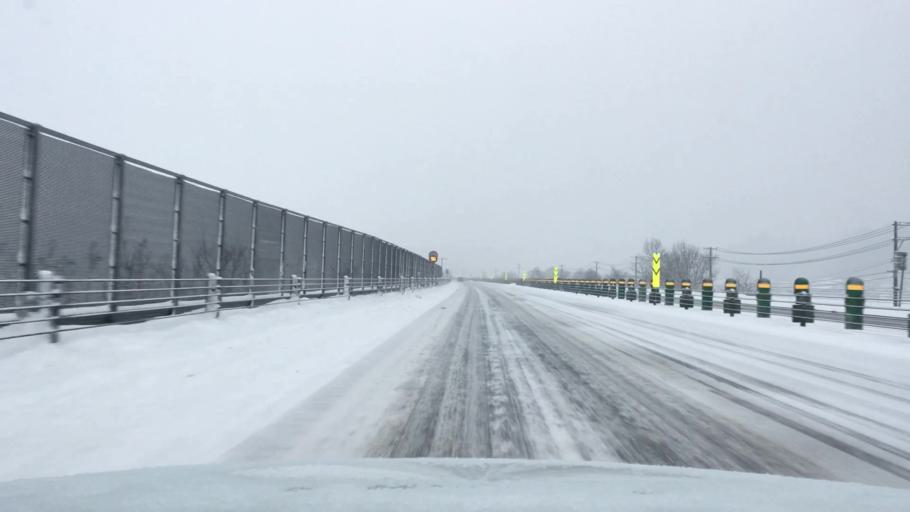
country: JP
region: Akita
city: Hanawa
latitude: 40.2863
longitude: 140.7594
